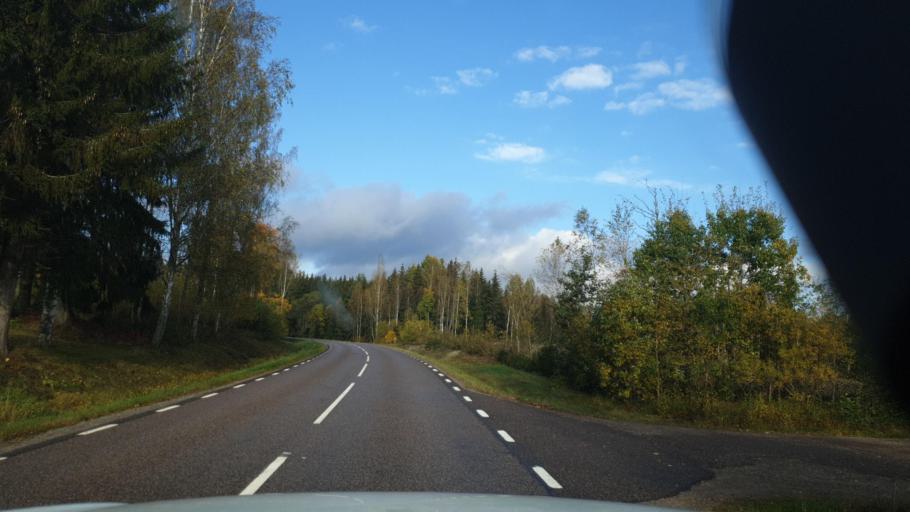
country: SE
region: Vaermland
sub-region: Arvika Kommun
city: Arvika
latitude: 59.5027
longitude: 12.6805
